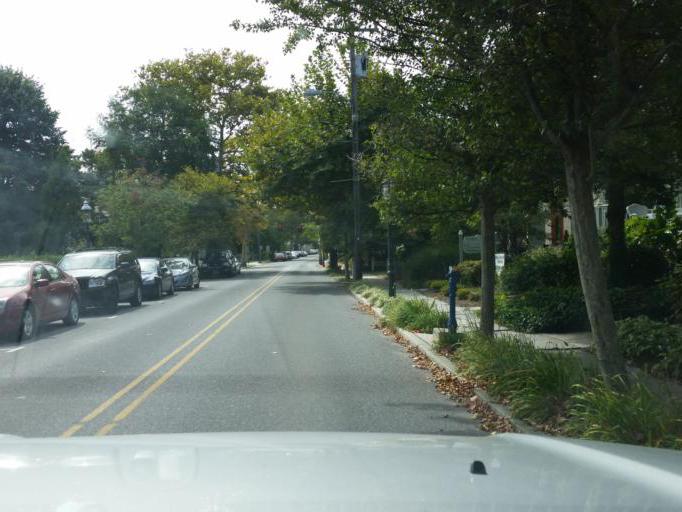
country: US
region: New Jersey
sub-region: Cape May County
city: Cape May
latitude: 38.9360
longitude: -74.9190
